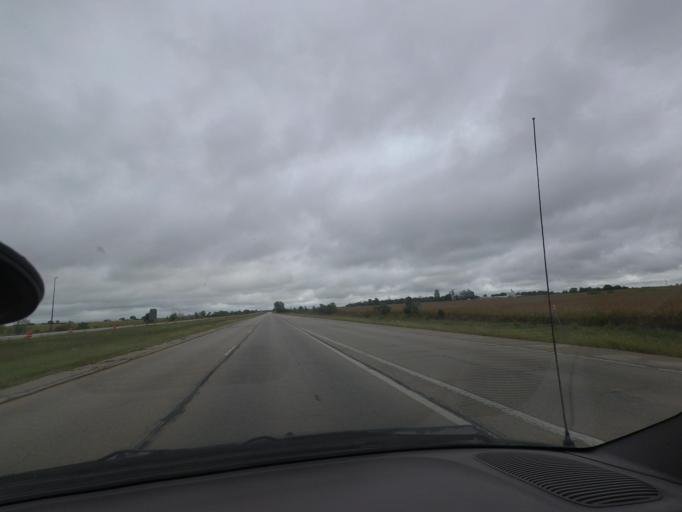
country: US
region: Illinois
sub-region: Piatt County
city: Cerro Gordo
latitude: 40.0168
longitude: -88.7407
